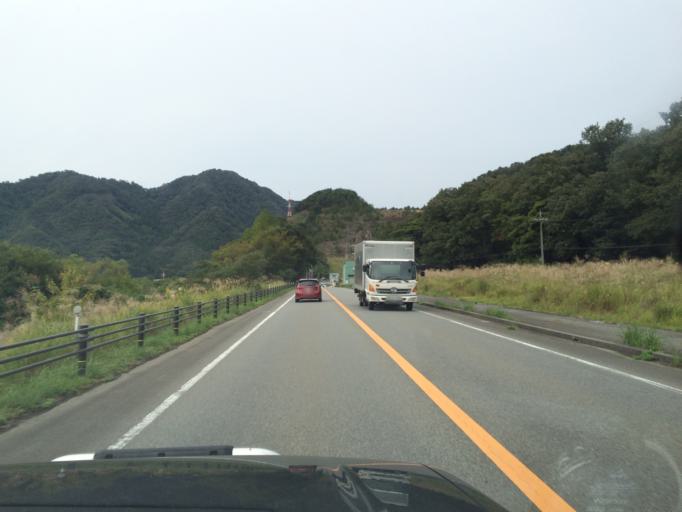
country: JP
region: Hyogo
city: Toyooka
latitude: 35.4023
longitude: 134.7843
